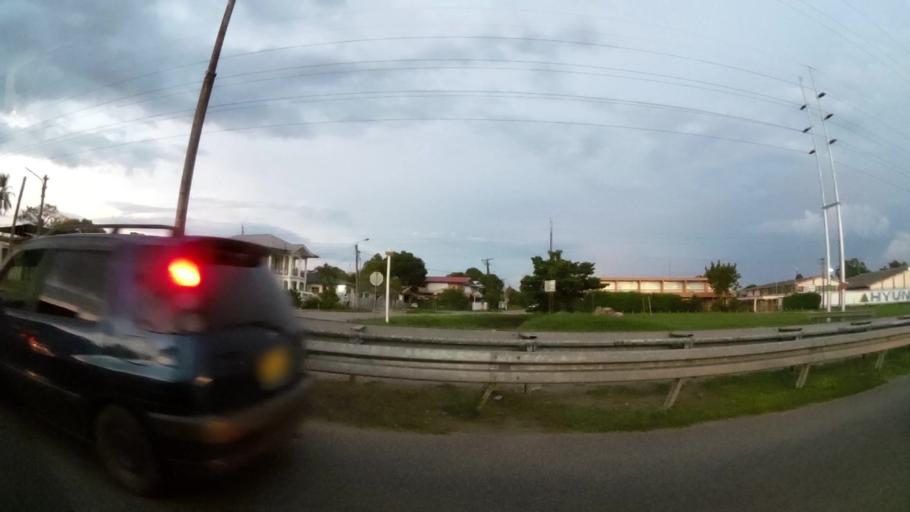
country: SR
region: Paramaribo
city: Paramaribo
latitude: 5.7959
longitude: -55.1769
